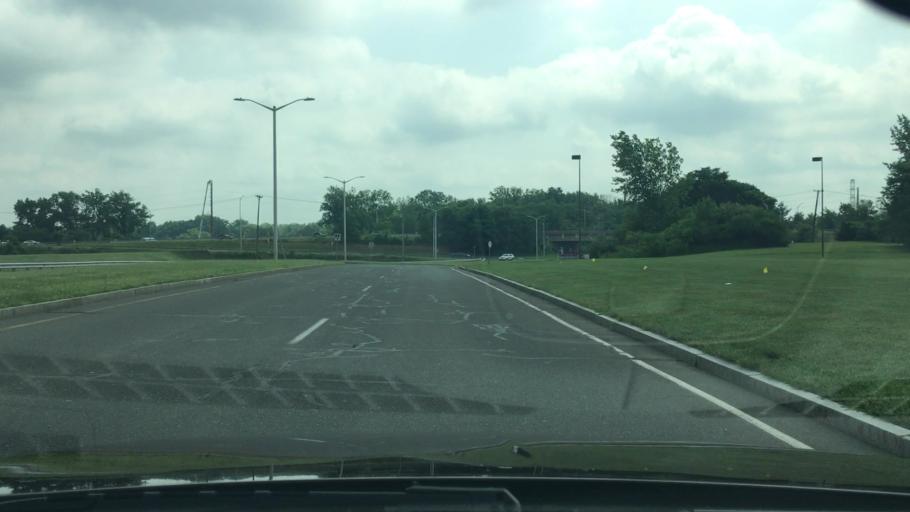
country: US
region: Connecticut
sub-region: Hartford County
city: Hartford
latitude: 41.7595
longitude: -72.6565
